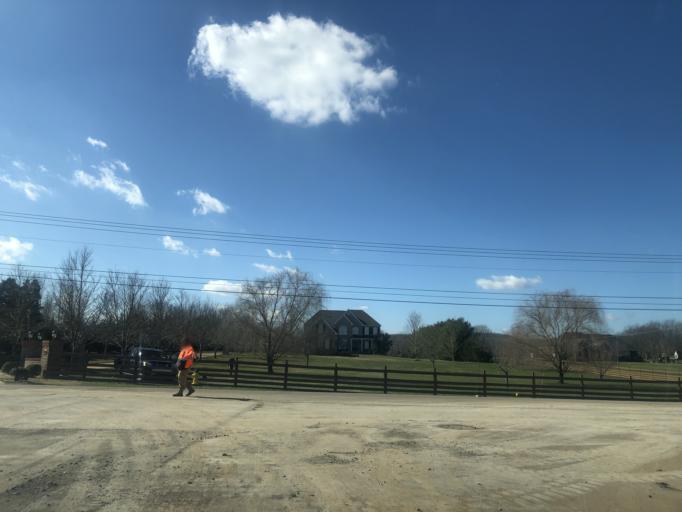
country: US
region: Tennessee
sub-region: Rutherford County
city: Smyrna
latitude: 35.8851
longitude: -86.4971
